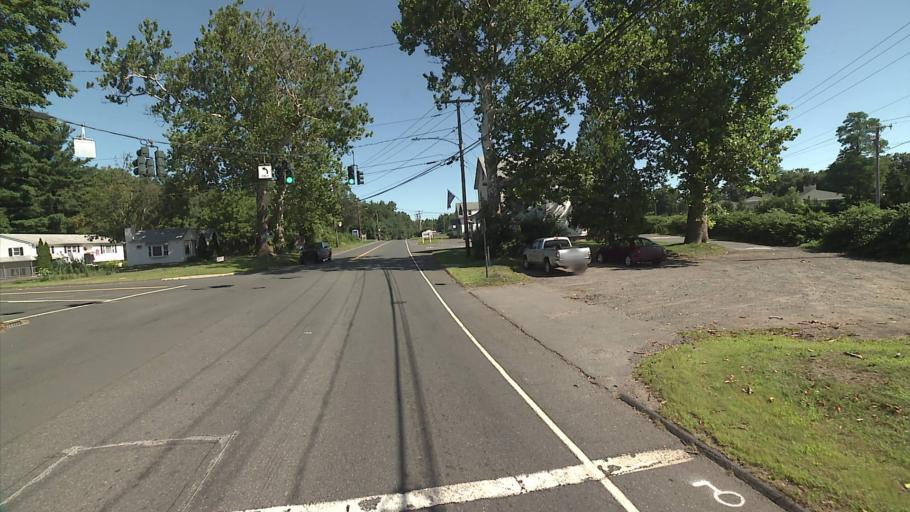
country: US
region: Connecticut
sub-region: Hartford County
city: Weatogue
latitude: 41.8496
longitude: -72.8129
